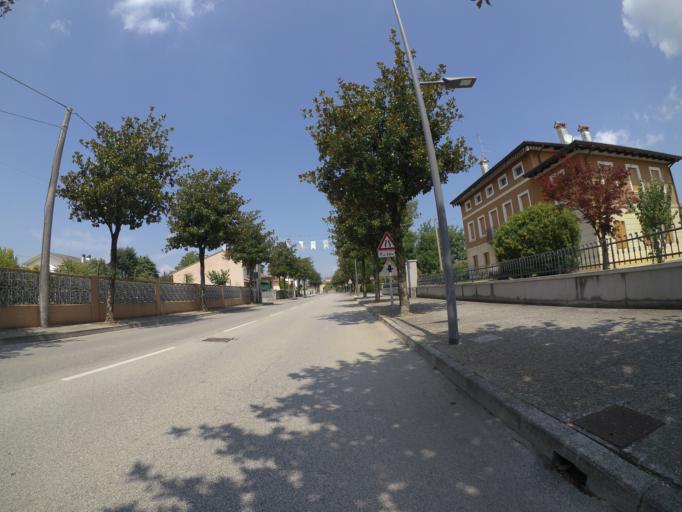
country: IT
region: Friuli Venezia Giulia
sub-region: Provincia di Udine
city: Codroipo
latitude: 45.9734
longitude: 12.9737
